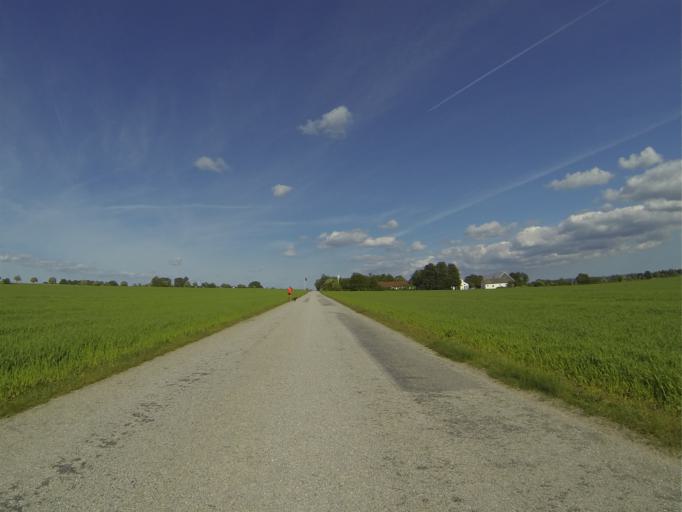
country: SE
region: Skane
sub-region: Lunds Kommun
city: Lund
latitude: 55.6866
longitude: 13.2448
